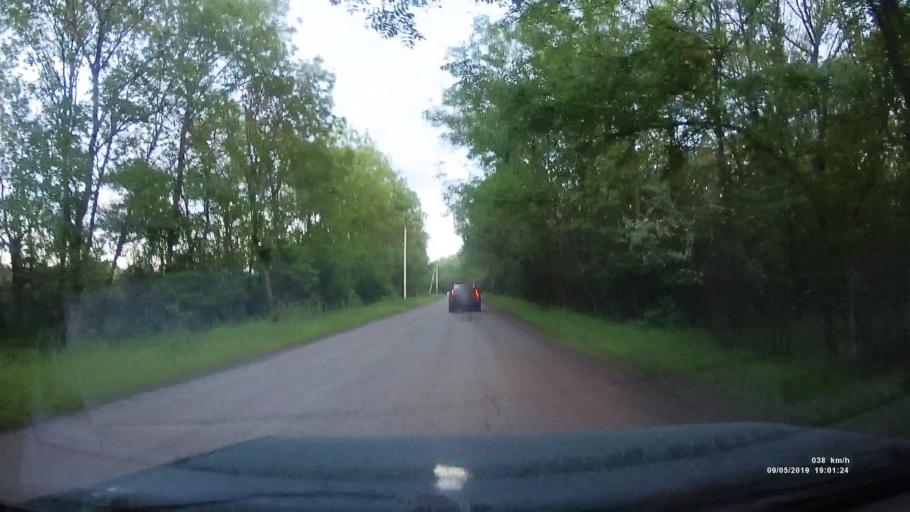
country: RU
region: Krasnodarskiy
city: Kanelovskaya
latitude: 46.7483
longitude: 39.1435
